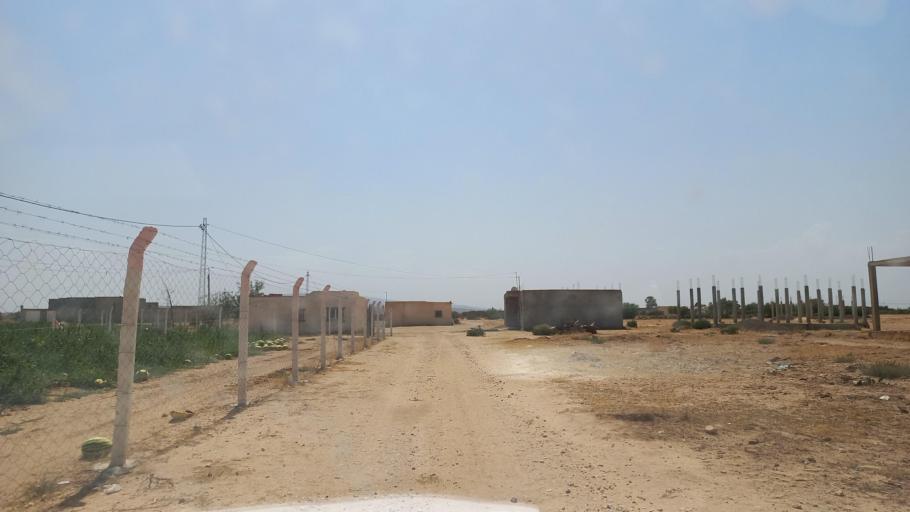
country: TN
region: Al Qasrayn
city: Kasserine
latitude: 35.2536
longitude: 9.0240
